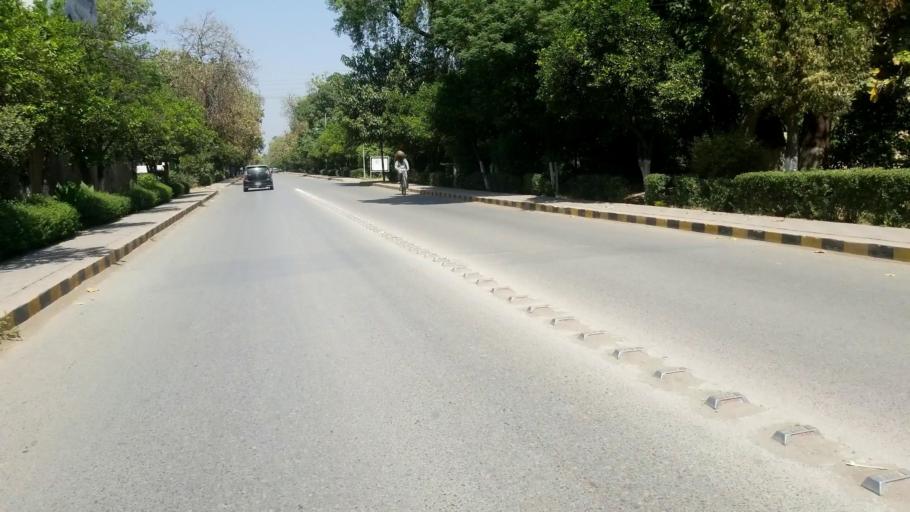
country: PK
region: Khyber Pakhtunkhwa
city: Peshawar
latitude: 34.0000
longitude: 71.4862
